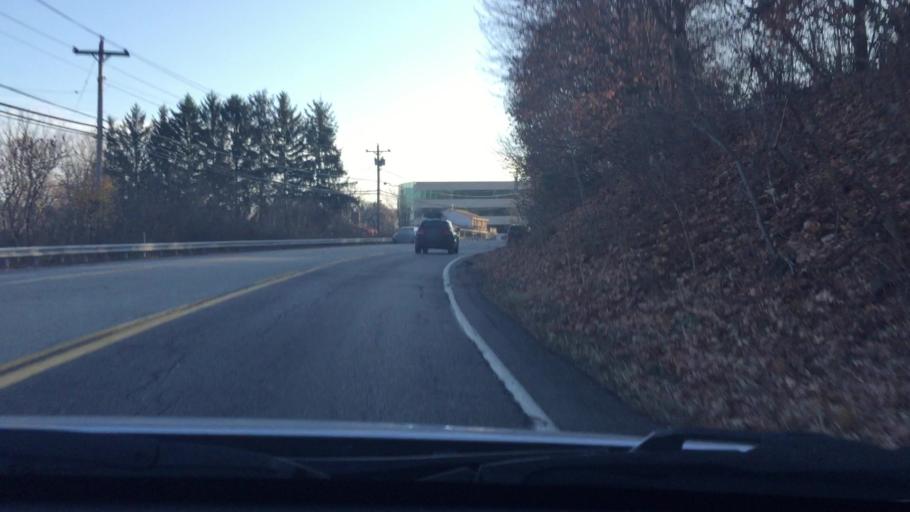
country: US
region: Pennsylvania
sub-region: Allegheny County
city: Bradford Woods
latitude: 40.6124
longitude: -80.0894
